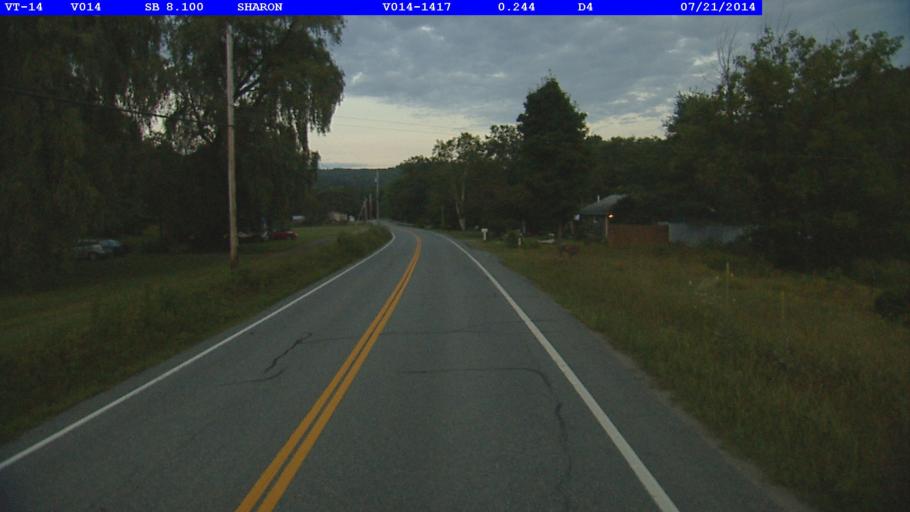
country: US
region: Vermont
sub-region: Windsor County
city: Wilder
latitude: 43.7241
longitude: -72.4302
